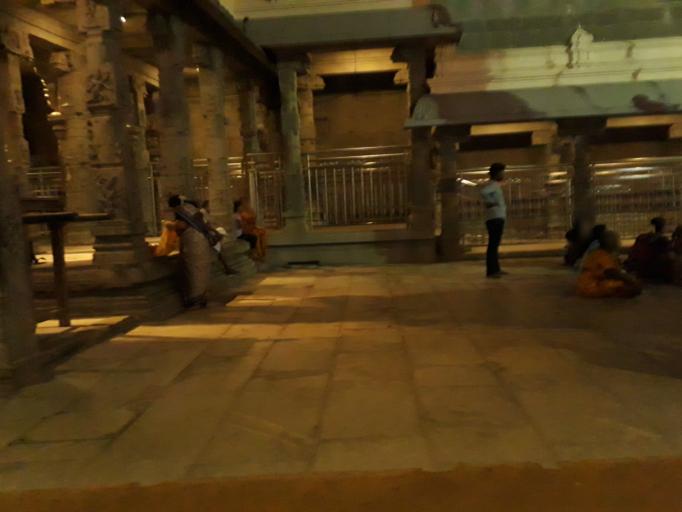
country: IN
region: Tamil Nadu
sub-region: Kancheepuram
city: Kanchipuram
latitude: 12.8403
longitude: 79.7034
